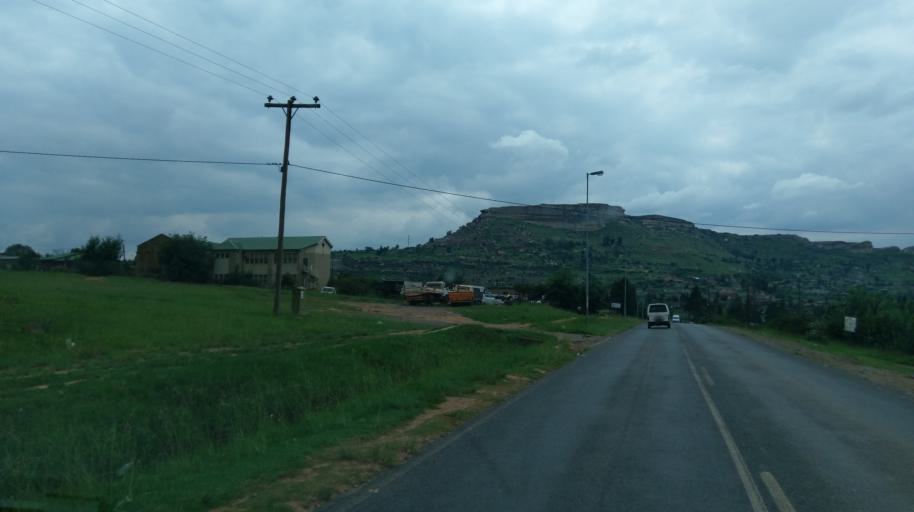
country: LS
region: Leribe
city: Leribe
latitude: -28.8693
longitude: 28.0594
